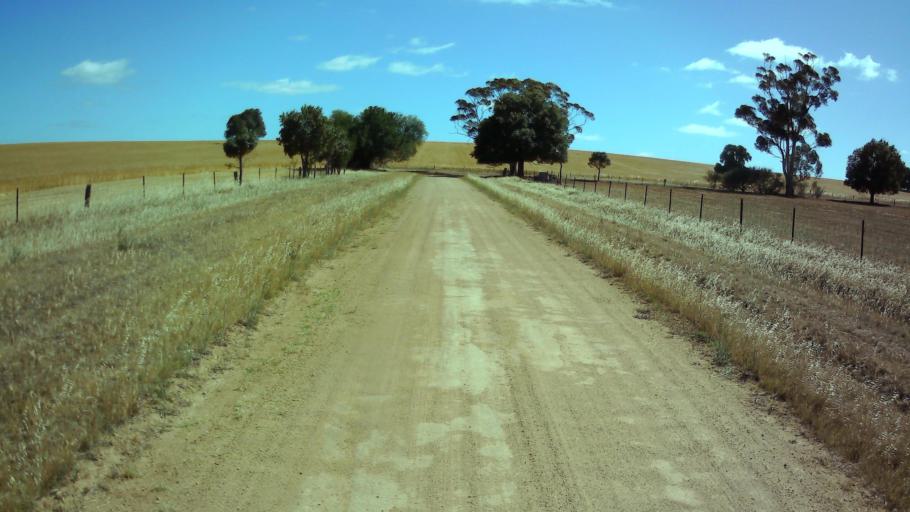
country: AU
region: New South Wales
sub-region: Weddin
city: Grenfell
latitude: -33.9658
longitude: 148.4109
